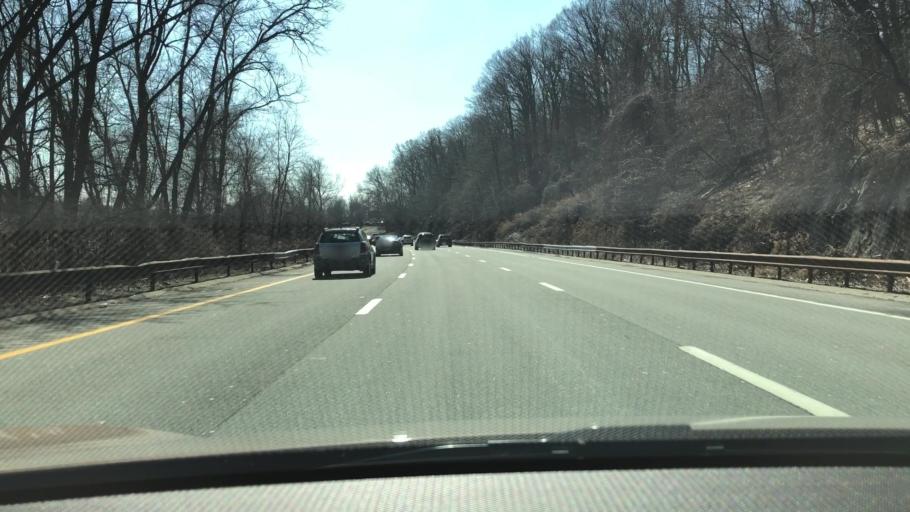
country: US
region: New York
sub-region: Westchester County
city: Tuckahoe
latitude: 40.9653
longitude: -73.8535
